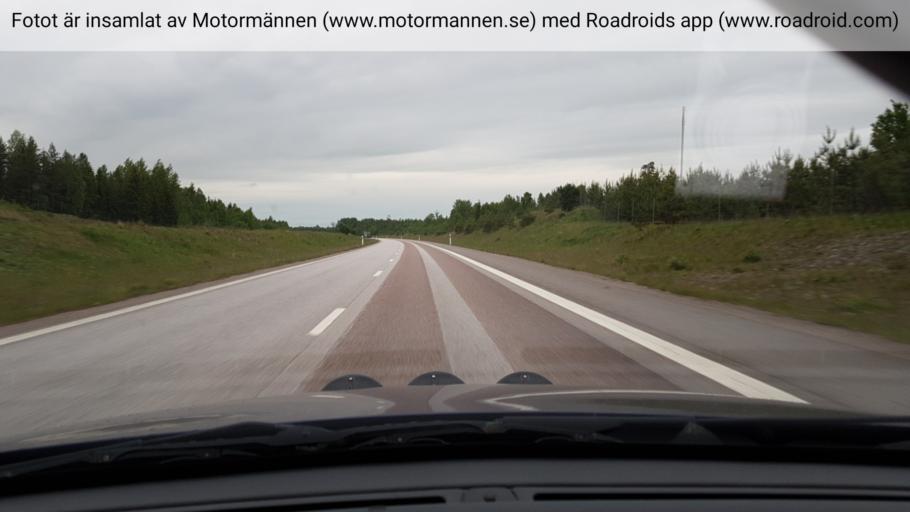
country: SE
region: Uppsala
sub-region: Osthammars Kommun
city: Bjorklinge
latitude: 60.0417
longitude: 17.6289
